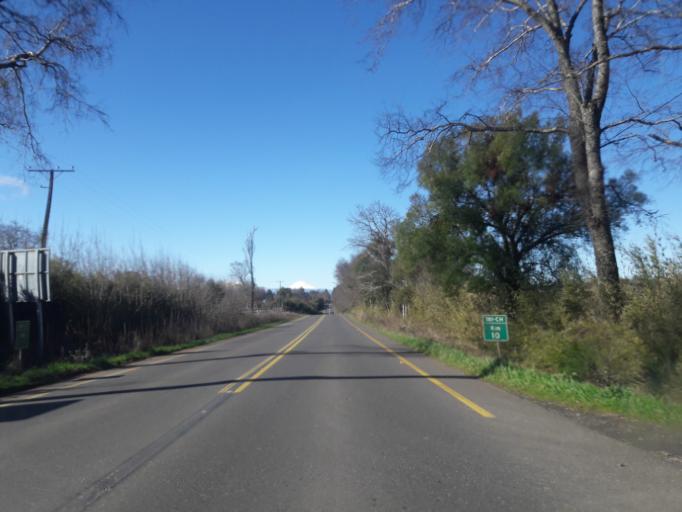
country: CL
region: Araucania
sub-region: Provincia de Malleco
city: Victoria
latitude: -38.2614
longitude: -72.2476
